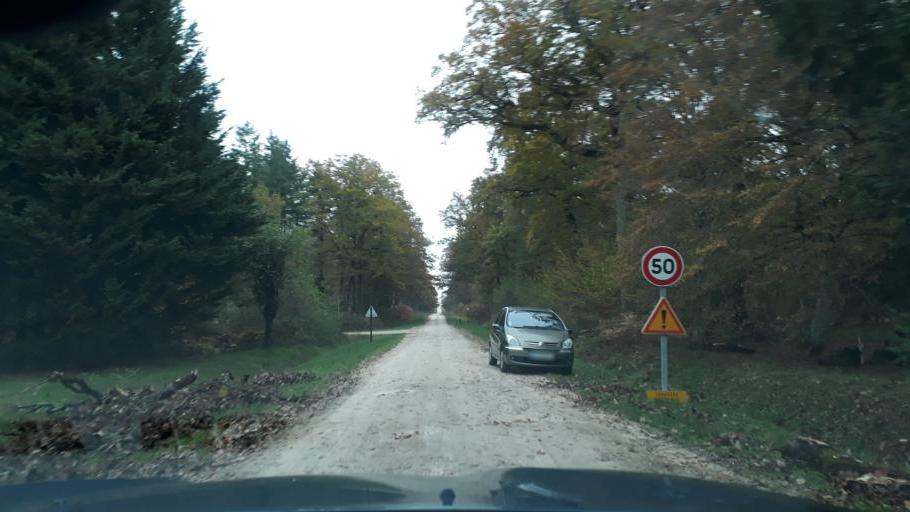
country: FR
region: Centre
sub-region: Departement du Loiret
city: Ouzouer-sur-Loire
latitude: 47.8253
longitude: 2.4847
